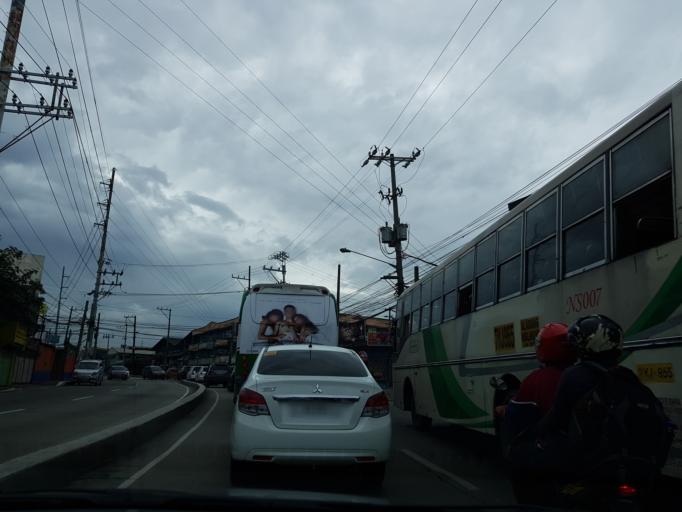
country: PH
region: Metro Manila
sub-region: Caloocan City
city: Niugan
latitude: 14.6683
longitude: 120.9821
